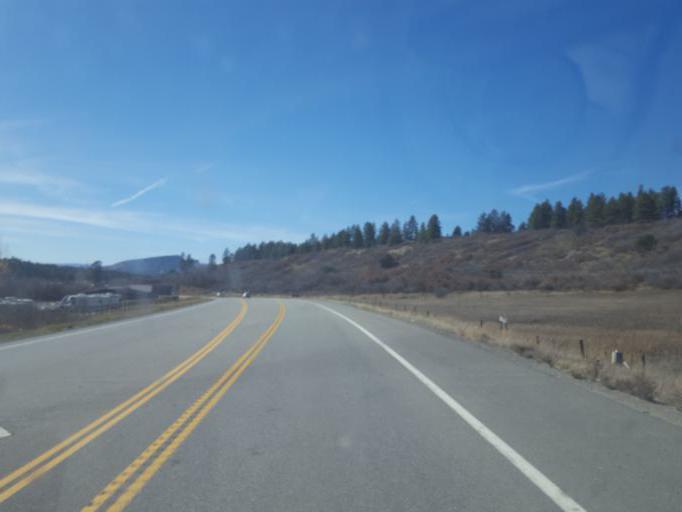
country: US
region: Colorado
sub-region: Archuleta County
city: Pagosa Springs
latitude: 37.2412
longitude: -107.1461
